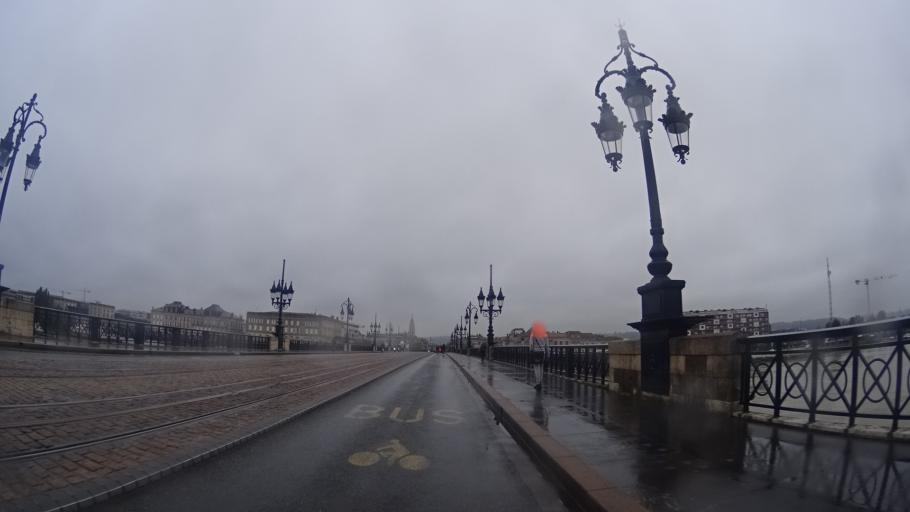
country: FR
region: Aquitaine
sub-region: Departement de la Gironde
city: Bordeaux
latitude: 44.8387
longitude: -0.5622
